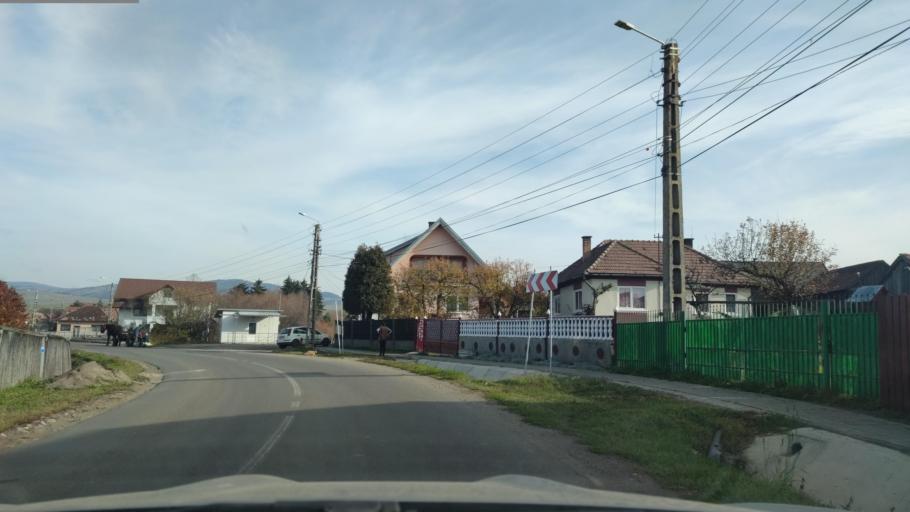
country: RO
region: Harghita
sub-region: Comuna Ditrau
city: Ditrau
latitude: 46.8137
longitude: 25.5206
